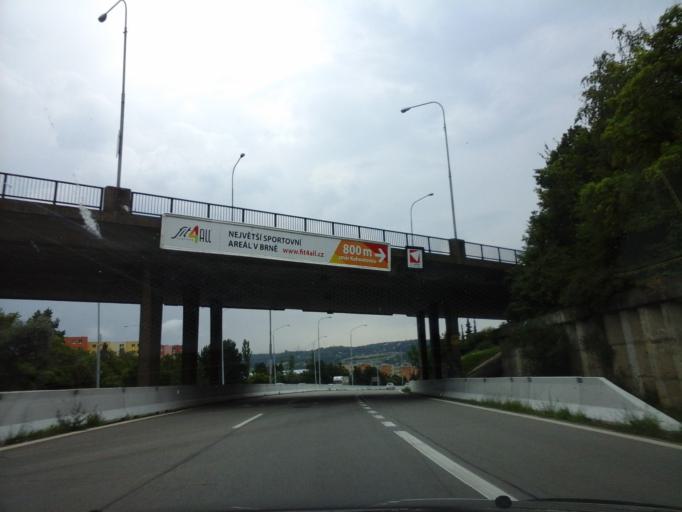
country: CZ
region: South Moravian
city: Ostopovice
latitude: 49.1744
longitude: 16.5621
